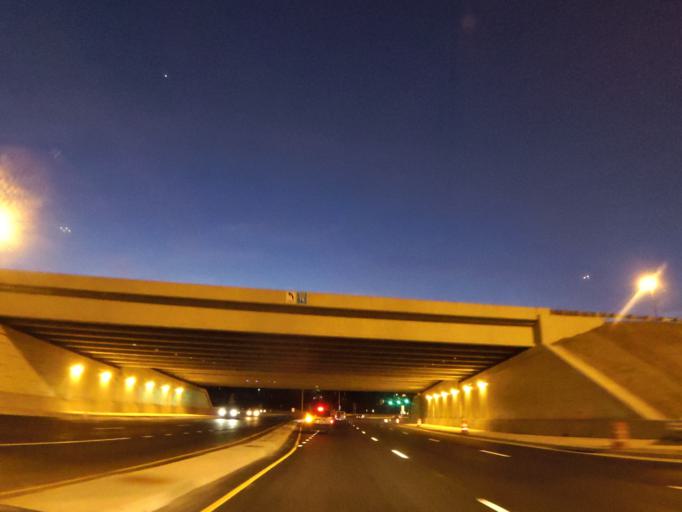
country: US
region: Georgia
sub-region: Whitfield County
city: Dalton
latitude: 34.7935
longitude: -85.0003
